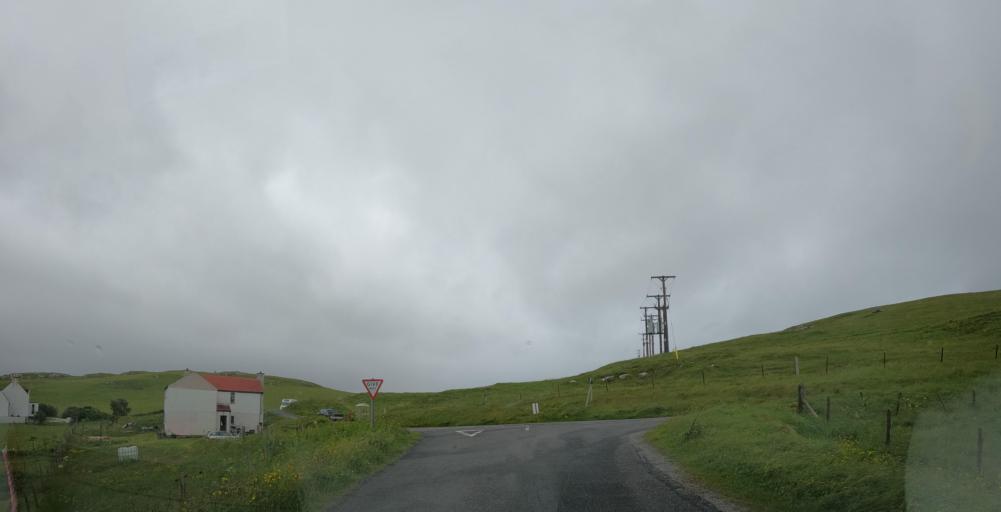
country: GB
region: Scotland
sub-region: Eilean Siar
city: Barra
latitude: 57.0347
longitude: -7.4295
